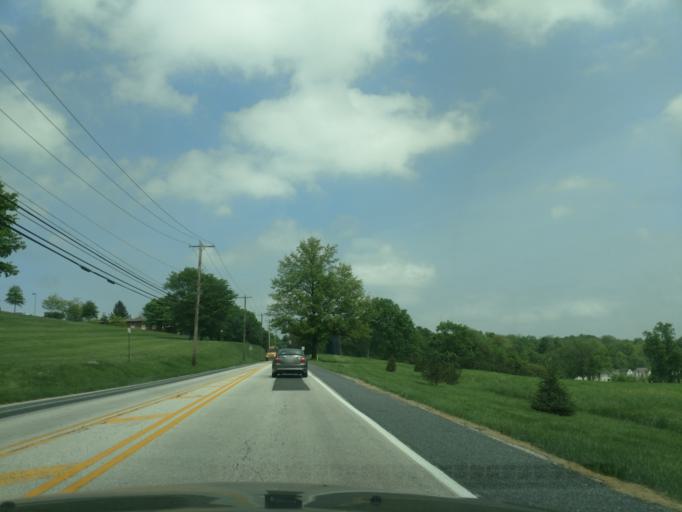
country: US
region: Pennsylvania
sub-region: Chester County
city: Kenilworth
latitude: 40.1752
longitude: -75.6577
